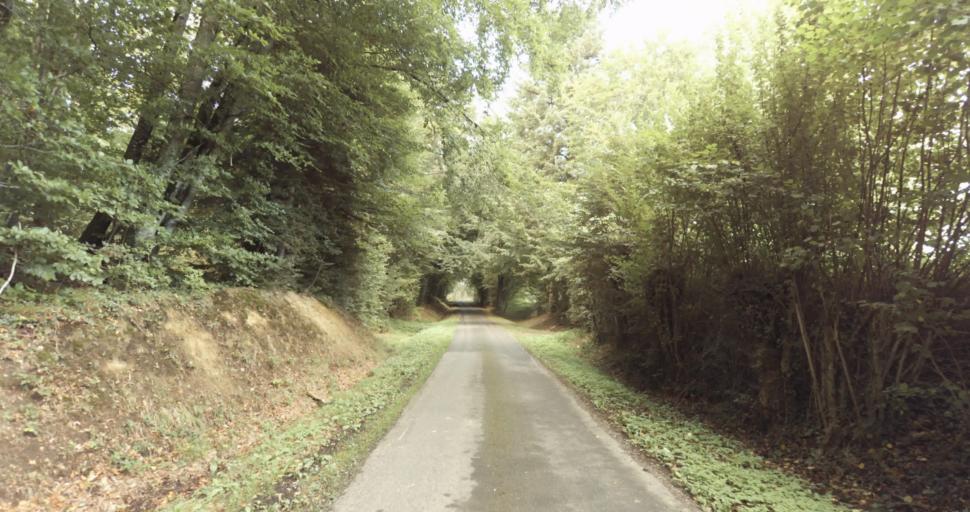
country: FR
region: Lower Normandy
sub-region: Departement de l'Orne
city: Sainte-Gauburge-Sainte-Colombe
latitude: 48.7530
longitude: 0.4133
